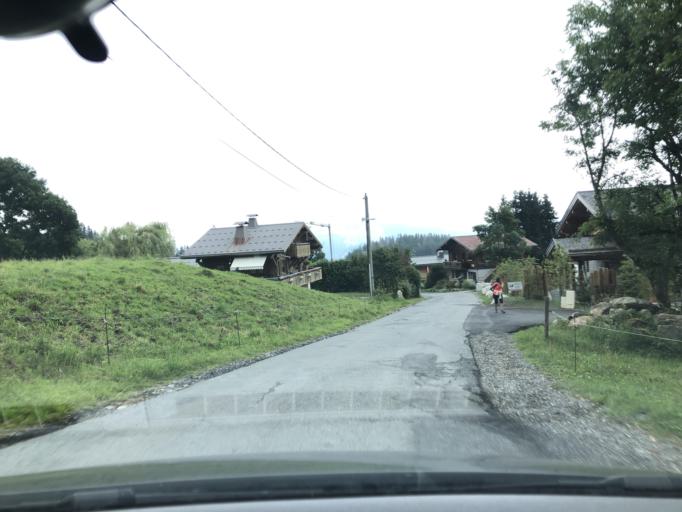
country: FR
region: Rhone-Alpes
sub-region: Departement de la Haute-Savoie
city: Combloux
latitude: 45.8984
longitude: 6.6188
